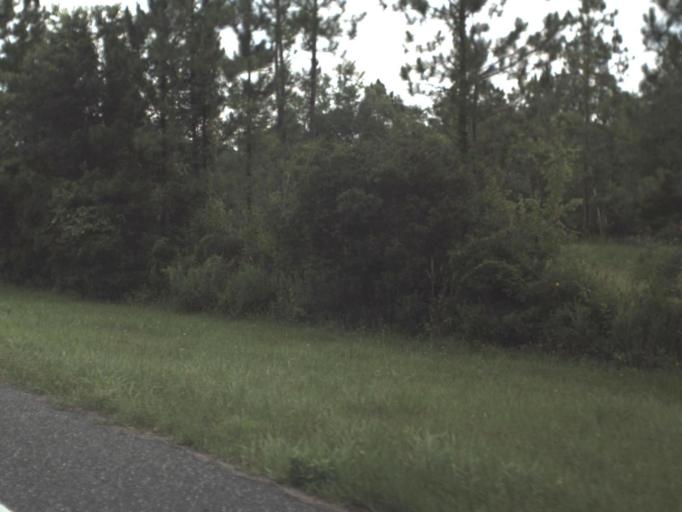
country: US
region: Florida
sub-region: Levy County
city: Bronson
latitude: 29.2969
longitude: -82.7498
